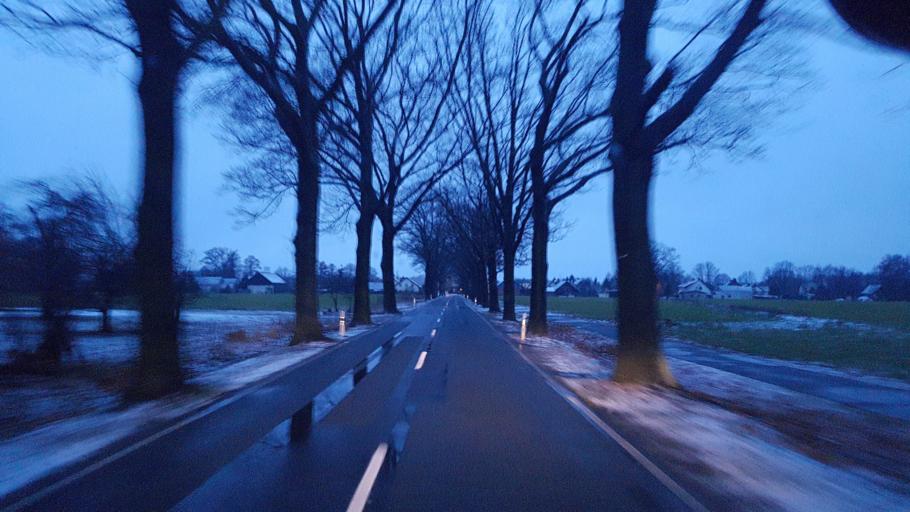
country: DE
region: Brandenburg
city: Briesen
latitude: 51.8287
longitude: 14.2697
